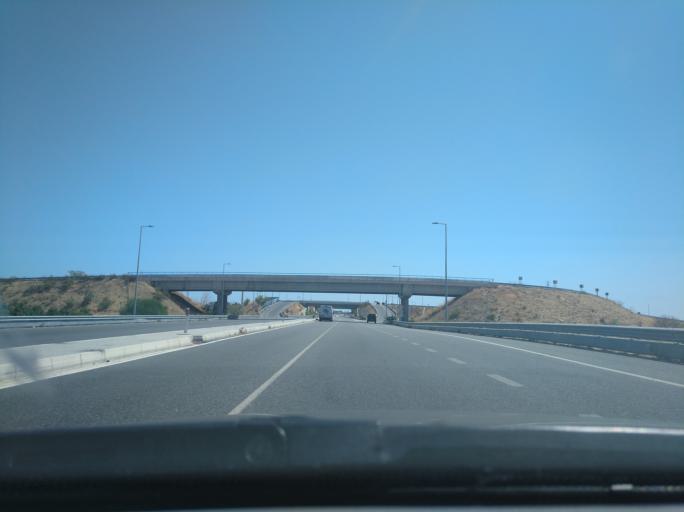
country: PT
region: Faro
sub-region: Faro
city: Faro
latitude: 37.0333
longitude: -7.9167
